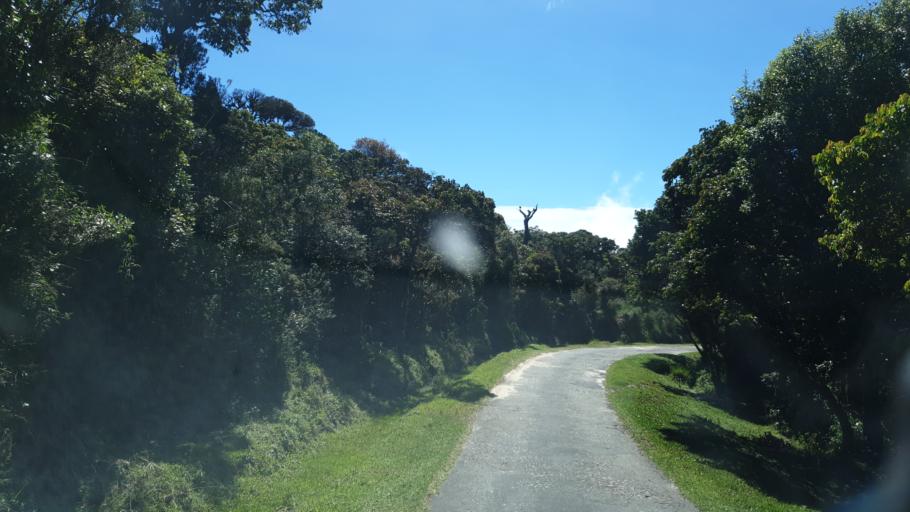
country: LK
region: Uva
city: Haputale
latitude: 6.8048
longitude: 80.8331
